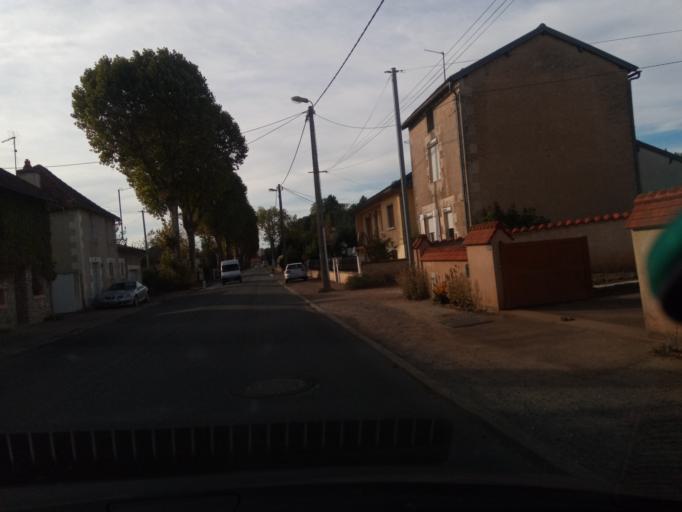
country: FR
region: Poitou-Charentes
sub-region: Departement de la Vienne
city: Montmorillon
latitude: 46.4195
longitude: 0.8769
